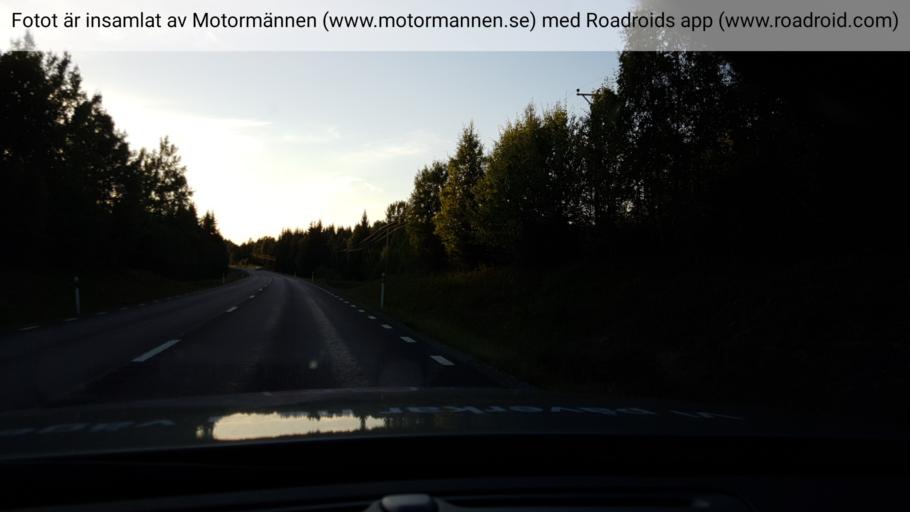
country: SE
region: Vaermland
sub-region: Storfors Kommun
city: Storfors
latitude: 59.4495
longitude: 14.3897
